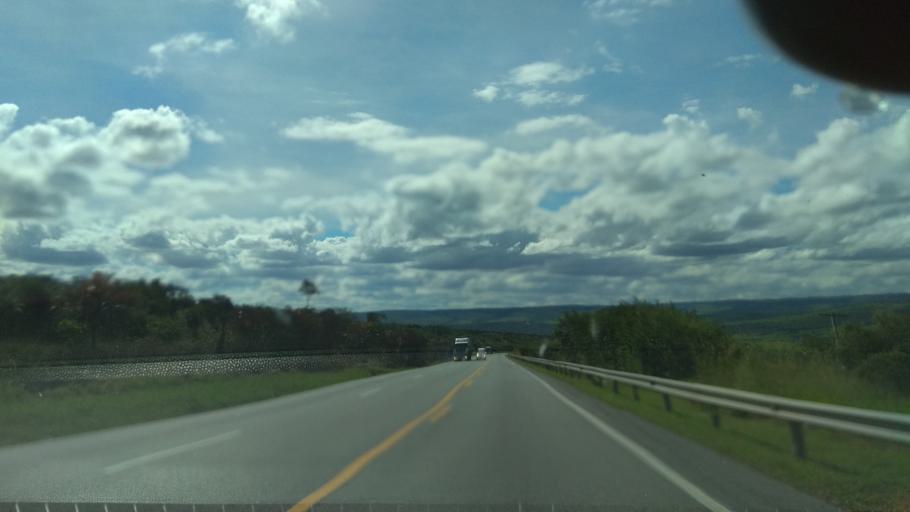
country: BR
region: Bahia
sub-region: Santa Ines
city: Santa Ines
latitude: -13.1878
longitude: -40.0061
